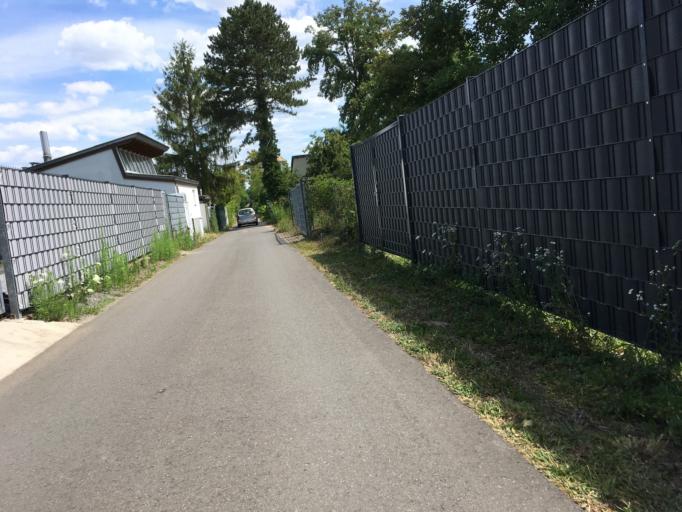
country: DE
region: Rheinland-Pfalz
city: Altrip
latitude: 49.4277
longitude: 8.4661
